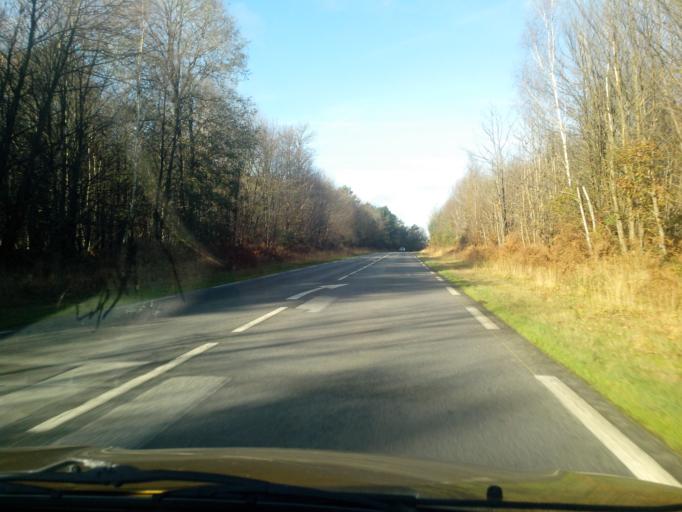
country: FR
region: Brittany
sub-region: Departement du Morbihan
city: Molac
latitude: 47.7660
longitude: -2.4494
